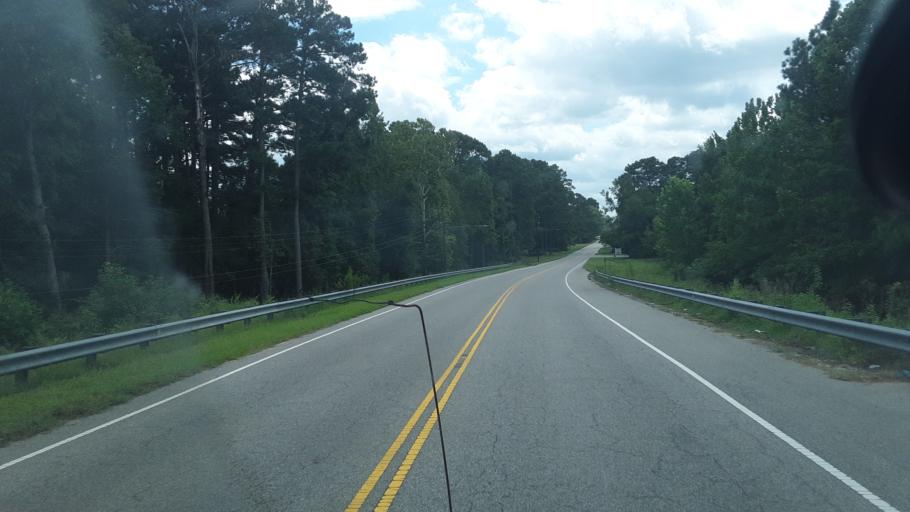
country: US
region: North Carolina
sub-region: Robeson County
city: Fairmont
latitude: 34.3069
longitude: -79.0431
